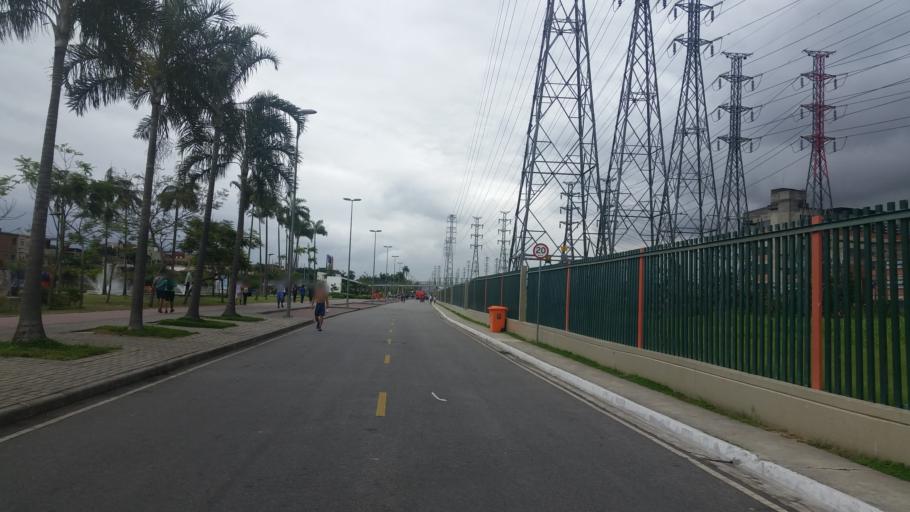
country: BR
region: Rio de Janeiro
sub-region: Sao Joao De Meriti
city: Sao Joao de Meriti
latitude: -22.8670
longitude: -43.3421
